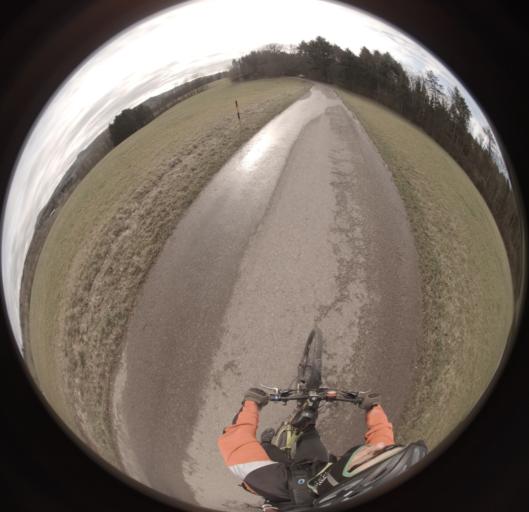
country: DE
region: Baden-Wuerttemberg
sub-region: Regierungsbezirk Stuttgart
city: Ottenbach
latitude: 48.7365
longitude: 9.7288
